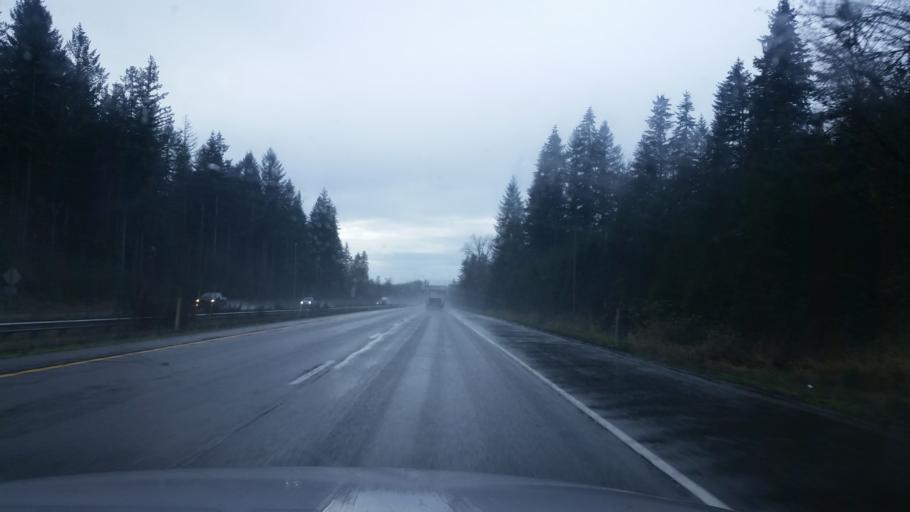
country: US
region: Washington
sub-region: King County
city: Hobart
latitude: 47.4218
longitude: -121.9995
